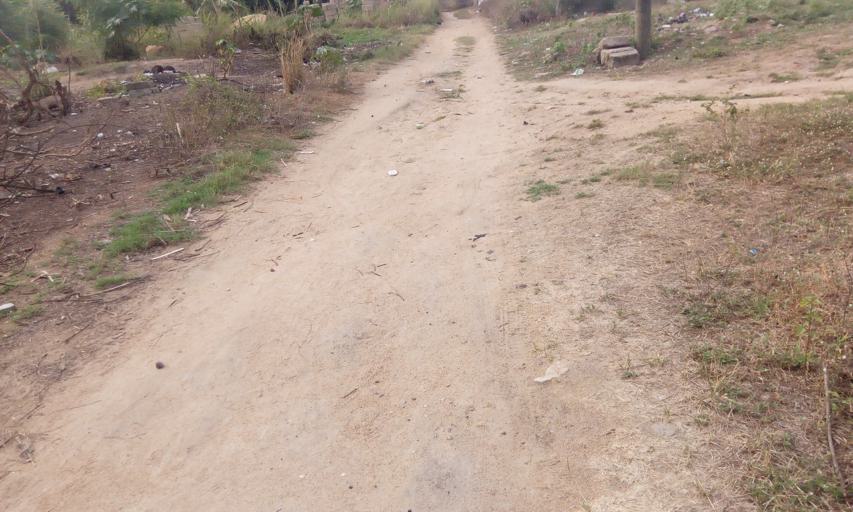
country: GH
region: Central
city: Winneba
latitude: 5.3563
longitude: -0.6288
